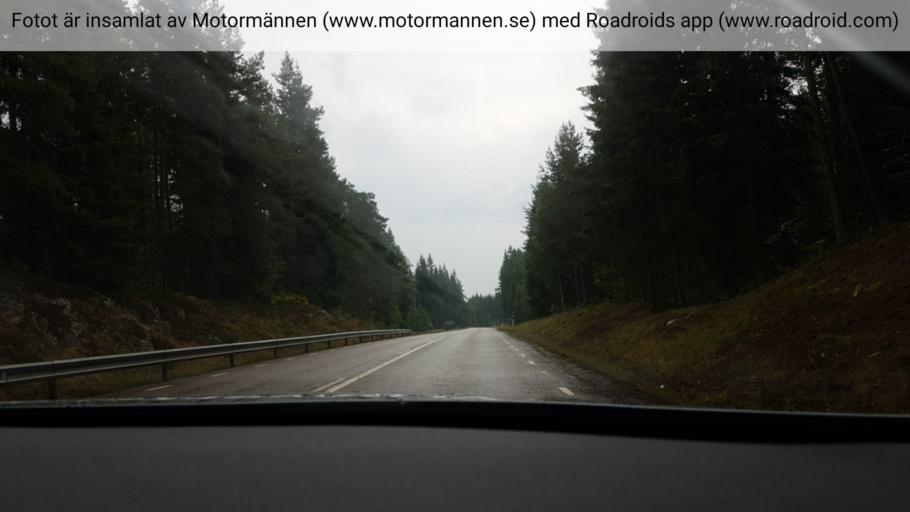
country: SE
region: Joenkoeping
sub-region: Vaggeryds Kommun
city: Vaggeryd
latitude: 57.5586
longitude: 14.2579
